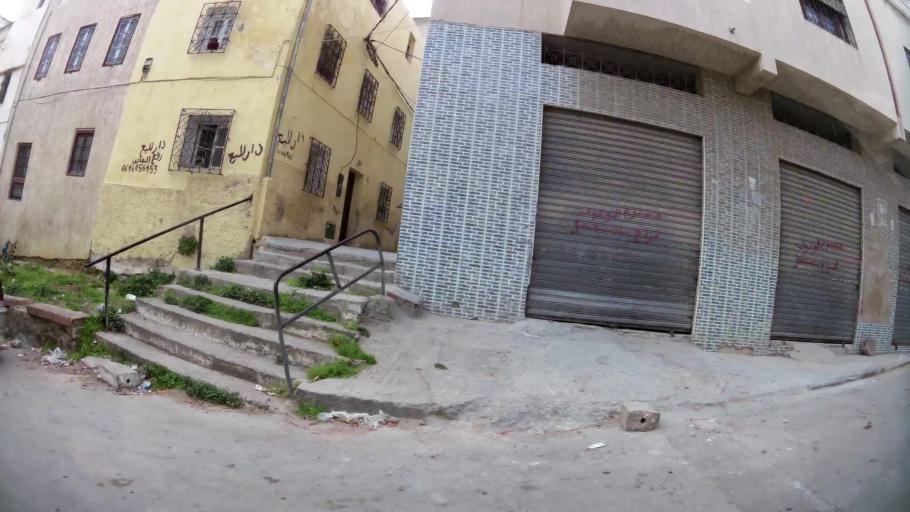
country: MA
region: Tanger-Tetouan
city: Tetouan
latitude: 35.5789
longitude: -5.3609
